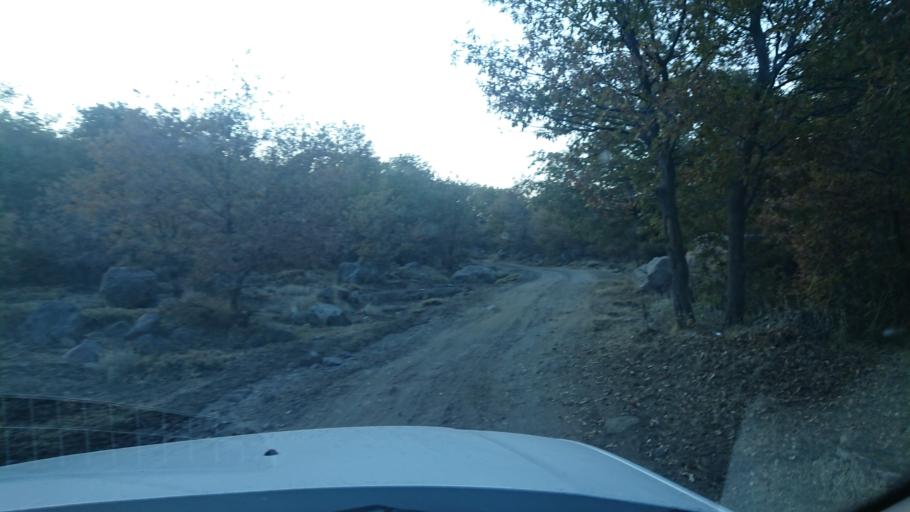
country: TR
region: Aksaray
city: Taspinar
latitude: 38.1646
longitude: 34.2097
